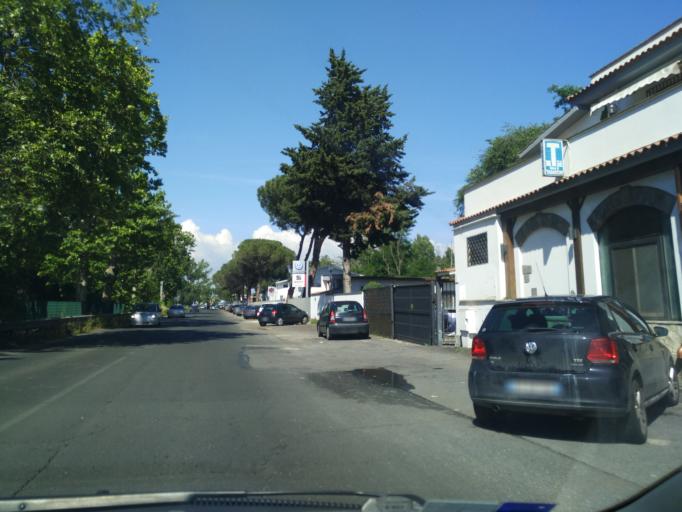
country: IT
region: Latium
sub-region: Citta metropolitana di Roma Capitale
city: Vitinia
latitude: 41.8202
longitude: 12.4371
